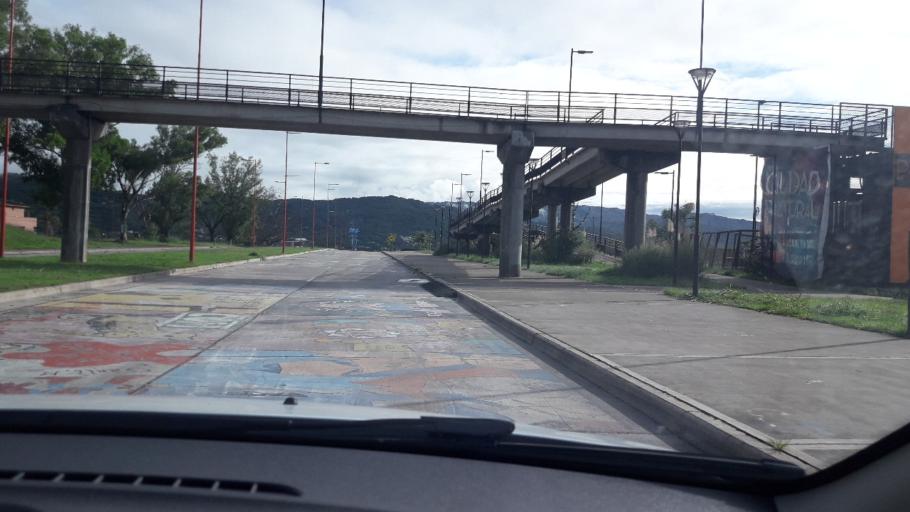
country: AR
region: Jujuy
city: San Salvador de Jujuy
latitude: -24.1821
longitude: -65.3306
